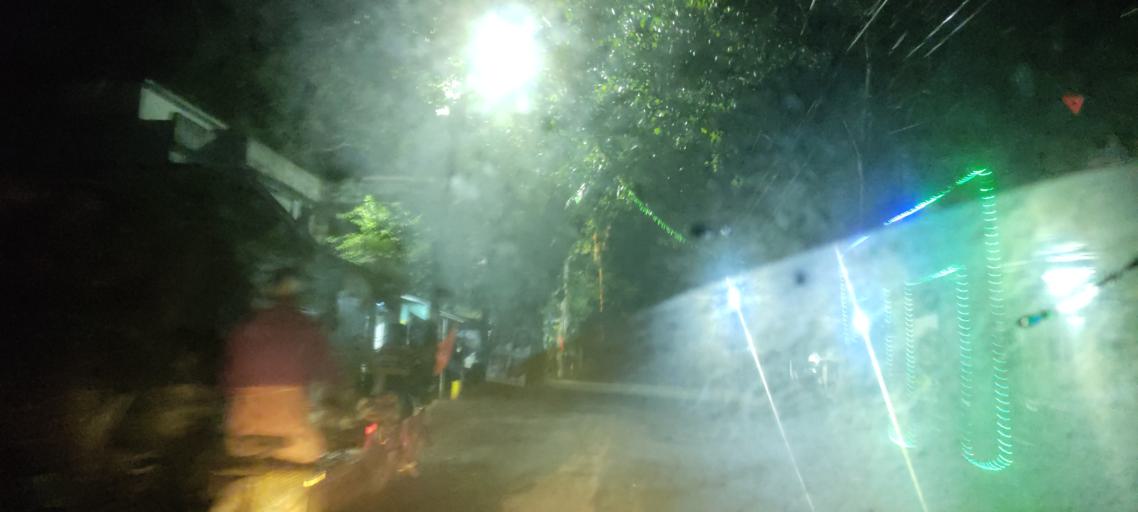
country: IN
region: Kerala
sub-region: Alappuzha
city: Vayalar
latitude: 9.7228
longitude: 76.3373
